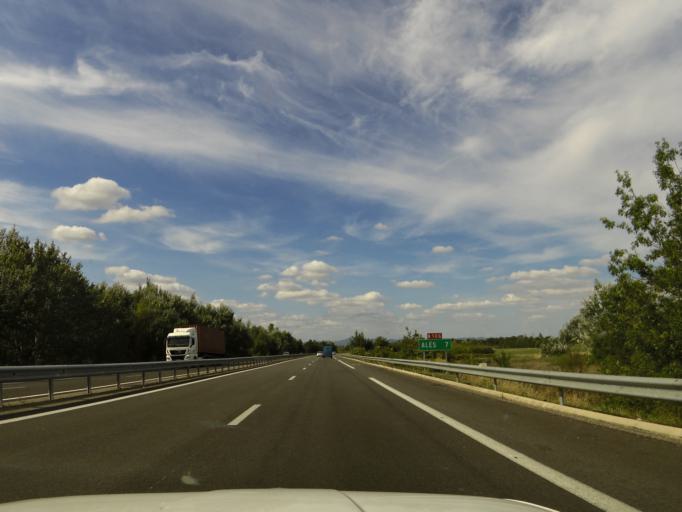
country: FR
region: Languedoc-Roussillon
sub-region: Departement du Gard
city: Saint-Hilaire-de-Brethmas
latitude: 44.0702
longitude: 4.1134
